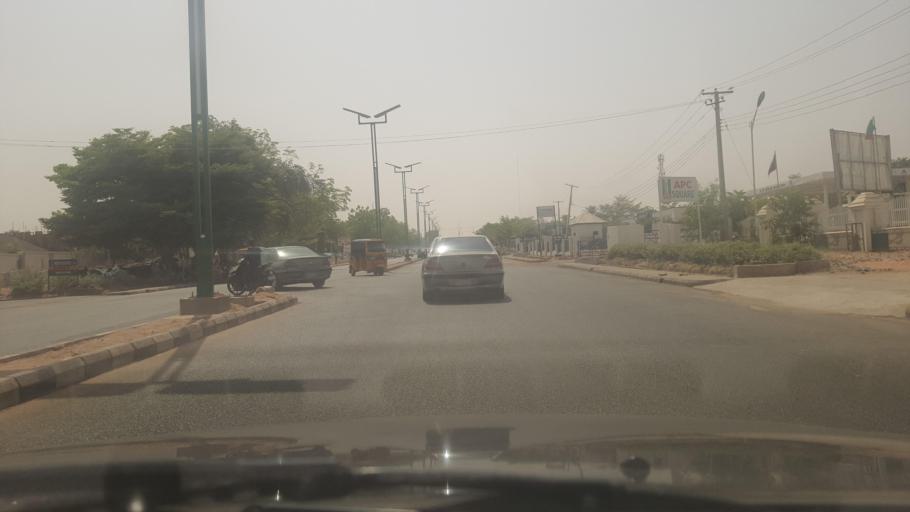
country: NG
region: Gombe
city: Gombe
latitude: 10.2855
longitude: 11.1438
